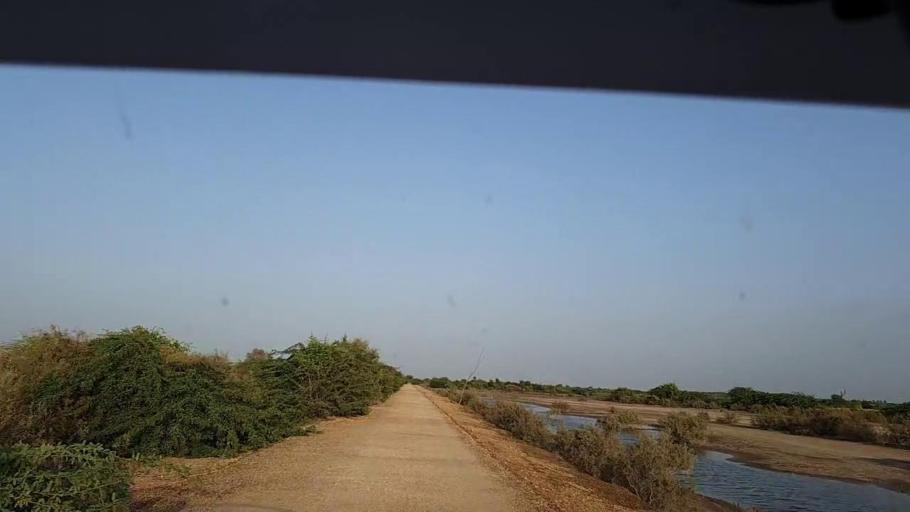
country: PK
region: Sindh
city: Kadhan
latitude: 24.5468
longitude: 68.9462
